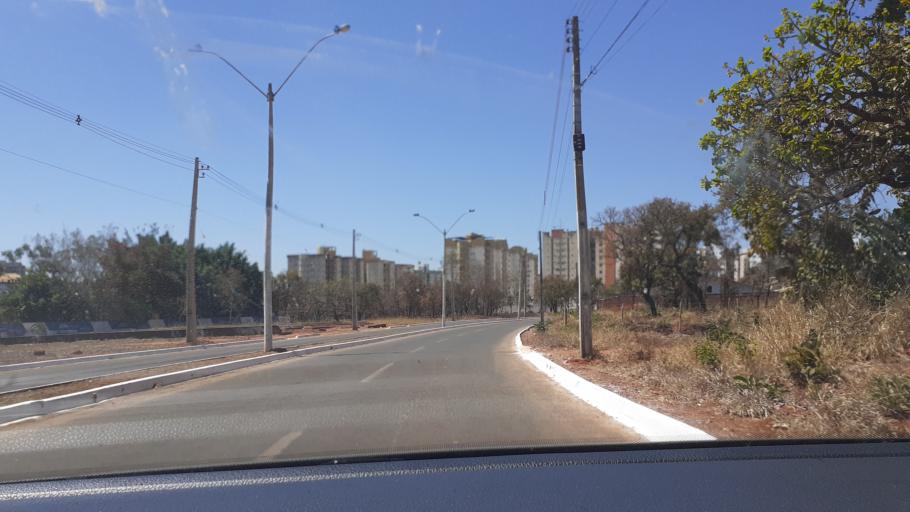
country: BR
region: Goias
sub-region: Caldas Novas
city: Caldas Novas
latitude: -17.7385
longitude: -48.6385
